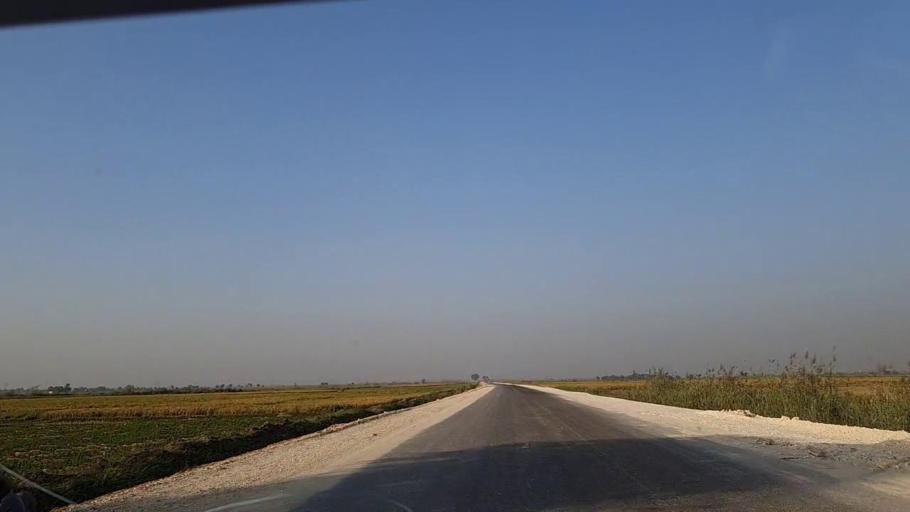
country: PK
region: Sindh
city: Rustam jo Goth
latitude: 27.9781
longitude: 68.8056
